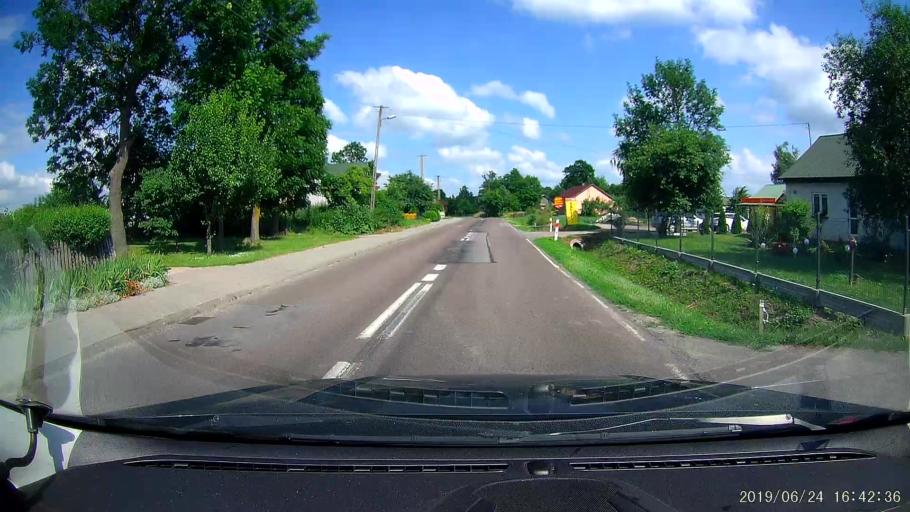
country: PL
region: Lublin Voivodeship
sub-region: Powiat tomaszowski
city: Michalow
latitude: 50.5350
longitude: 23.6189
